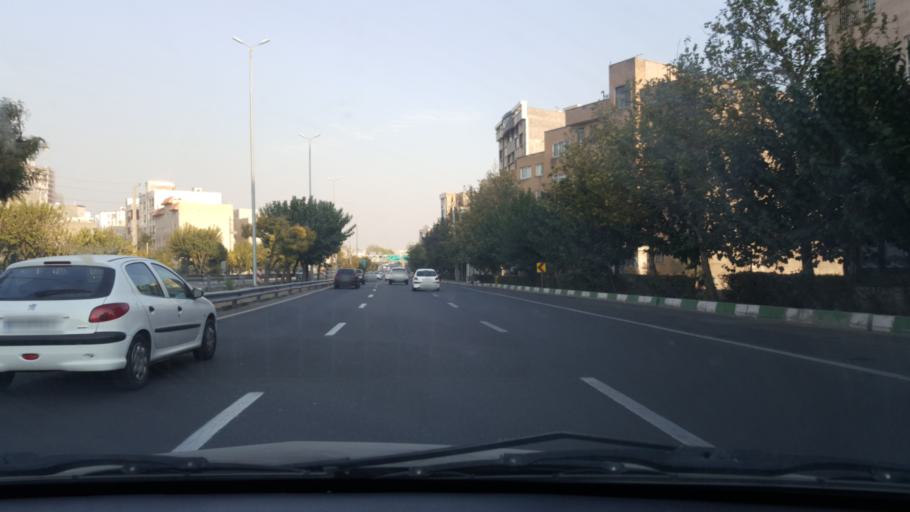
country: IR
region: Tehran
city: Tehran
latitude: 35.7332
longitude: 51.2877
